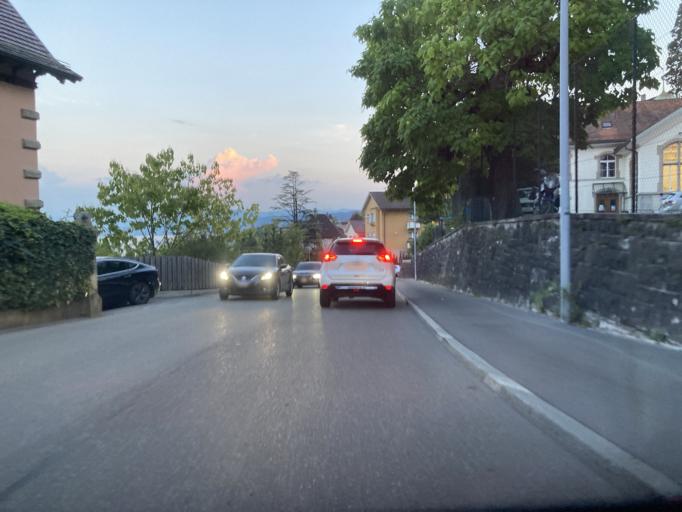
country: CH
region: Zurich
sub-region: Bezirk Horgen
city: Kilchberg
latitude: 47.3226
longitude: 8.5473
